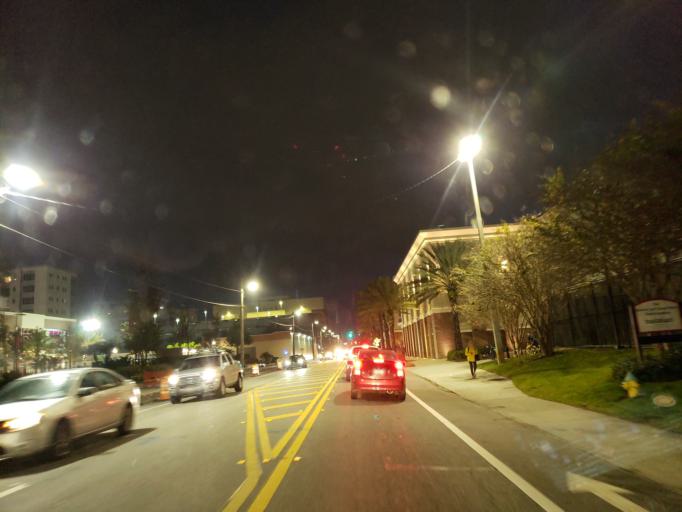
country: US
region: Florida
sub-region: Hillsborough County
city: Tampa
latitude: 27.9479
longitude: -82.4685
